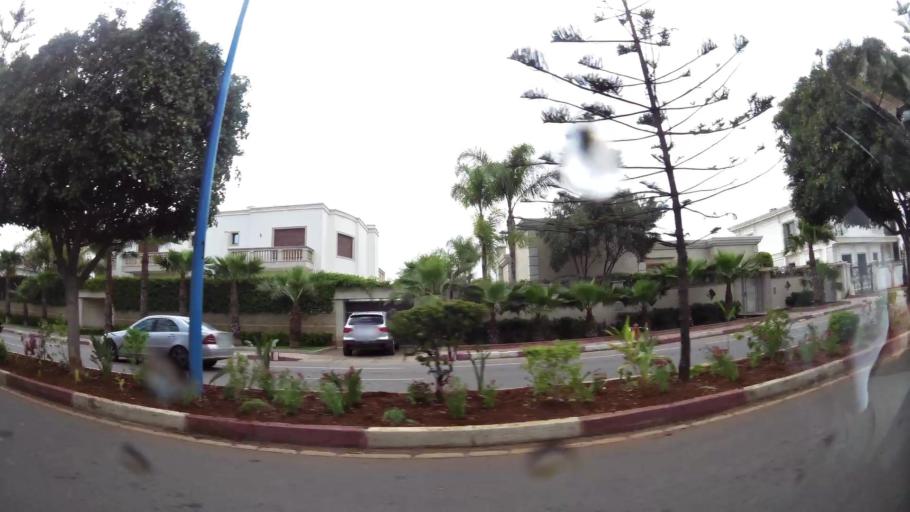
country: MA
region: Grand Casablanca
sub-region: Casablanca
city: Casablanca
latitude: 33.5448
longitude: -7.6314
